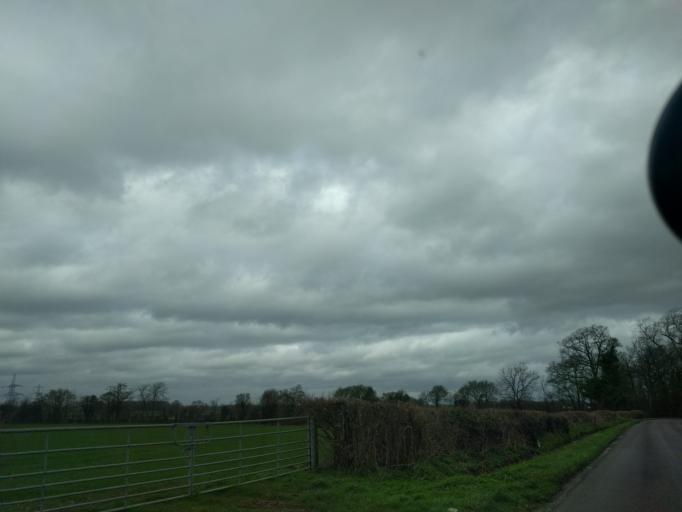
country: GB
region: England
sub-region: Wiltshire
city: Biddestone
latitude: 51.4987
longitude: -2.1950
